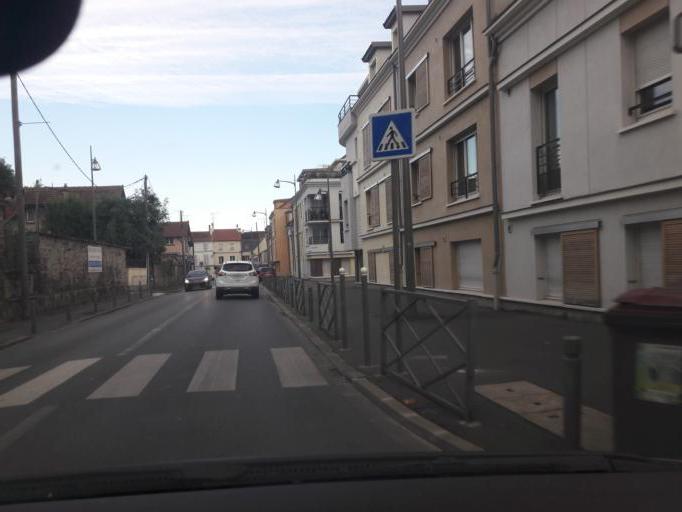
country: FR
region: Ile-de-France
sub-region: Departement de l'Essonne
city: Longjumeau
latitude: 48.6931
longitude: 2.2948
